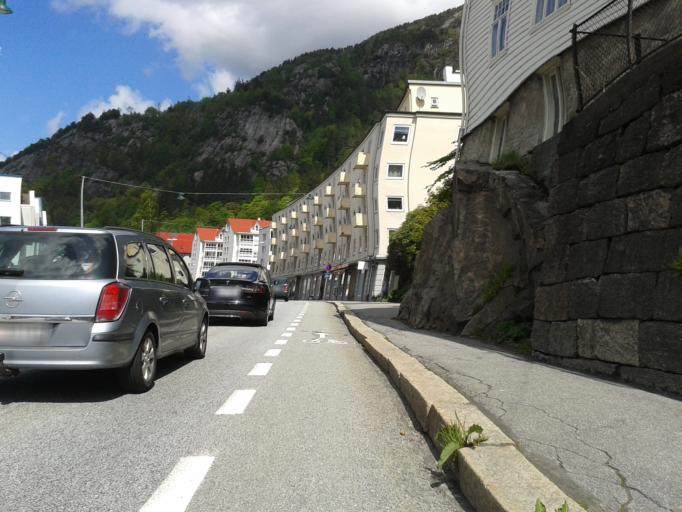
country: NO
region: Hordaland
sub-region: Bergen
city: Bergen
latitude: 60.4106
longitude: 5.3233
